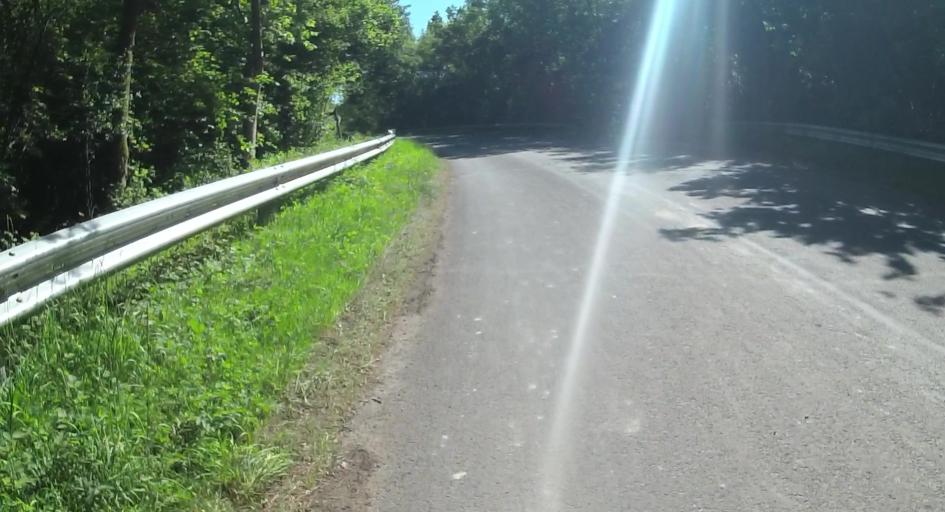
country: GB
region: England
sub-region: Hampshire
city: Old Basing
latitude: 51.2683
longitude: -0.9998
